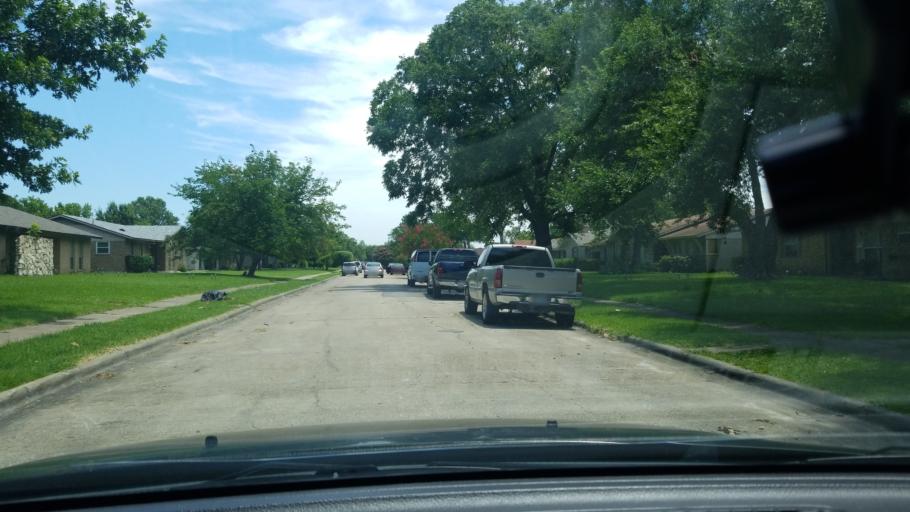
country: US
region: Texas
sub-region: Dallas County
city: Mesquite
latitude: 32.8081
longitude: -96.6516
